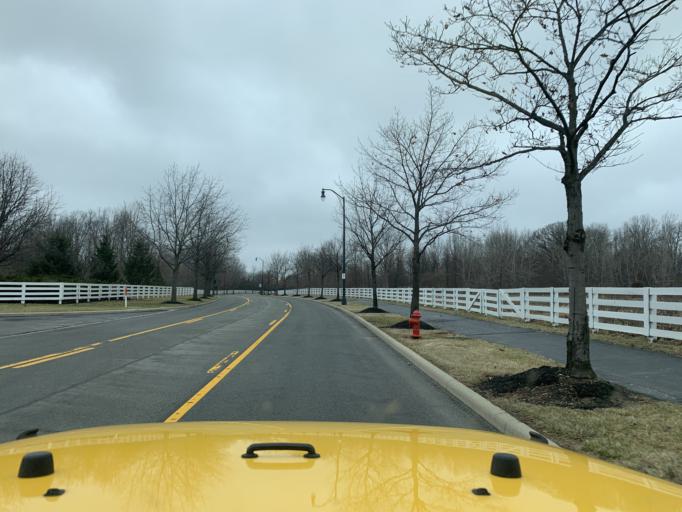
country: US
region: Ohio
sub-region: Franklin County
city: New Albany
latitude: 40.0917
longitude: -82.7966
